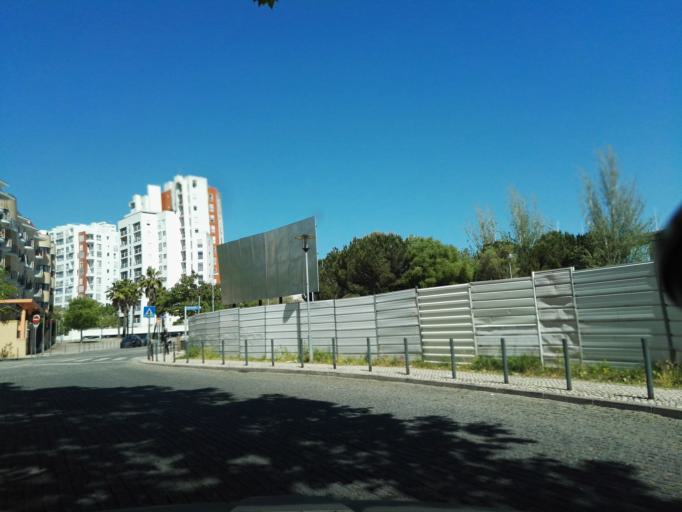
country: PT
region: Lisbon
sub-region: Loures
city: Moscavide
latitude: 38.7837
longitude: -9.0937
